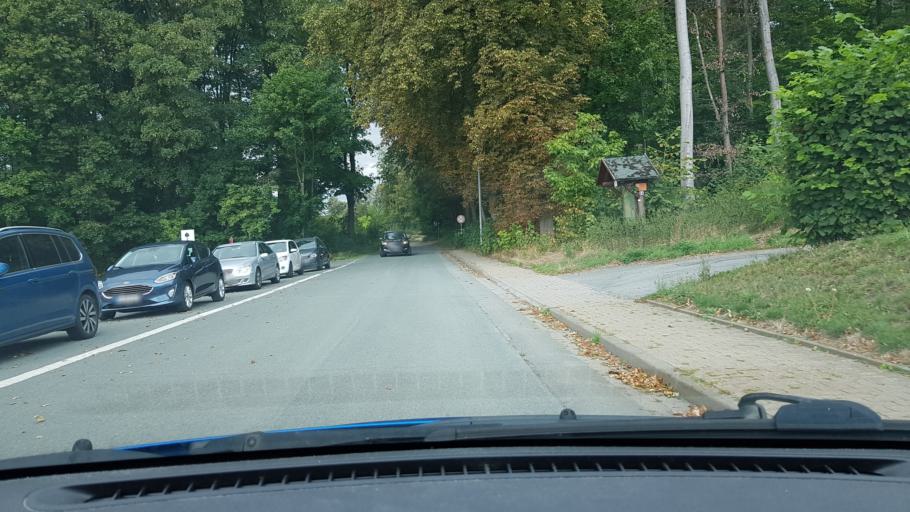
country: DE
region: Lower Saxony
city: Bad Munder am Deister
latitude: 52.2112
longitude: 9.4811
